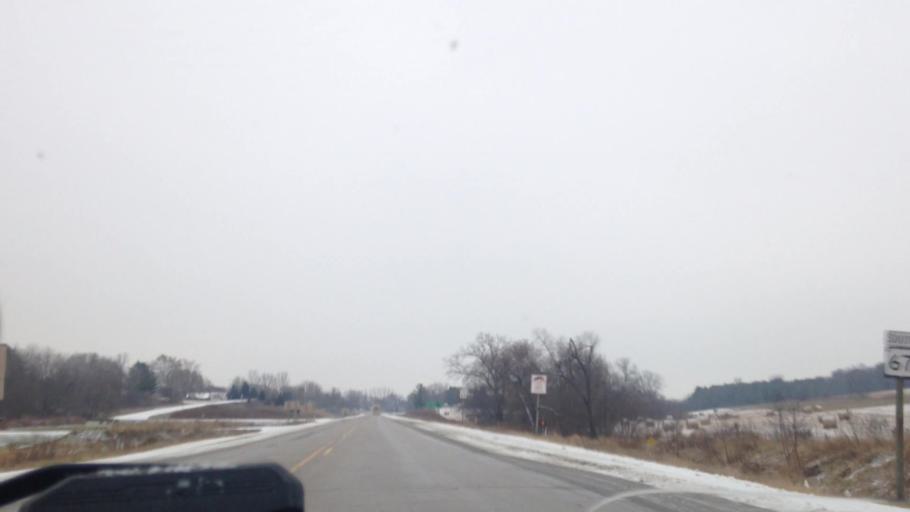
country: US
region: Wisconsin
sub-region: Dodge County
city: Mayville
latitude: 43.4425
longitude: -88.5440
